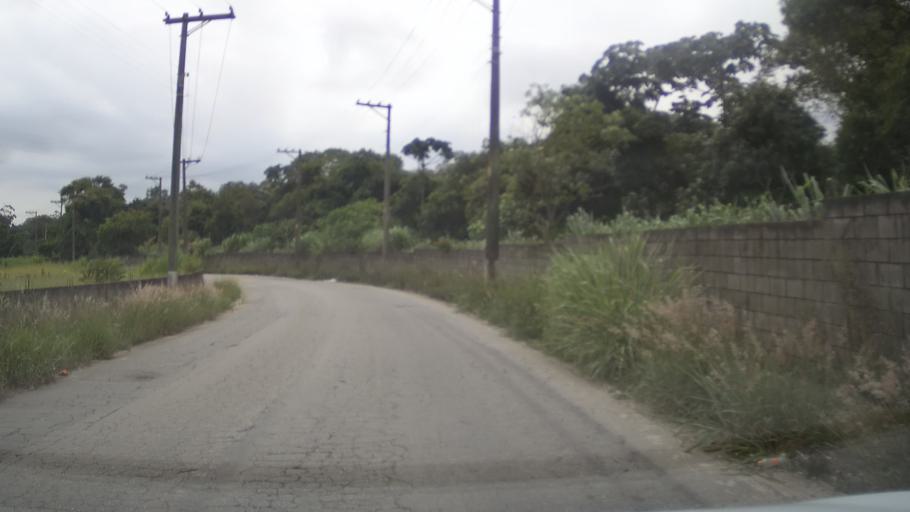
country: BR
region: Sao Paulo
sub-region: Itaquaquecetuba
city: Itaquaquecetuba
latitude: -23.4507
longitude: -46.3856
